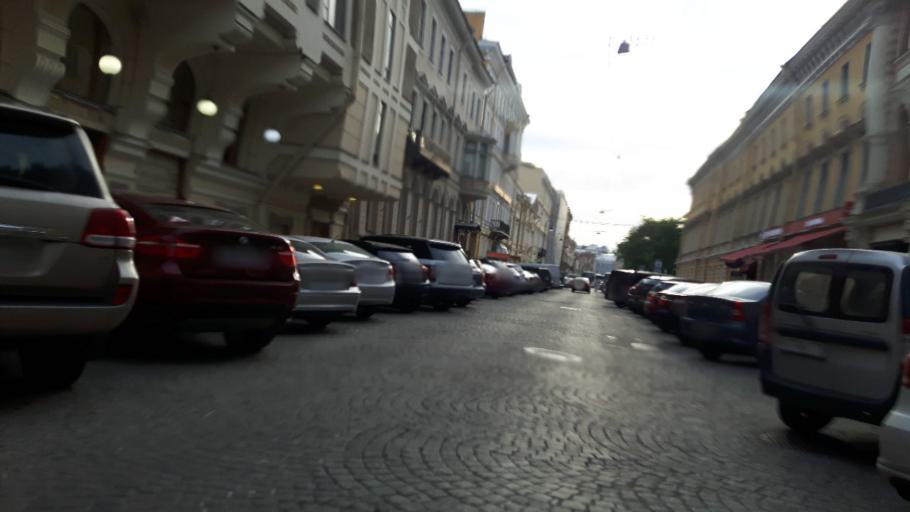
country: RU
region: St.-Petersburg
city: Saint Petersburg
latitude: 59.9362
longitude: 30.3353
